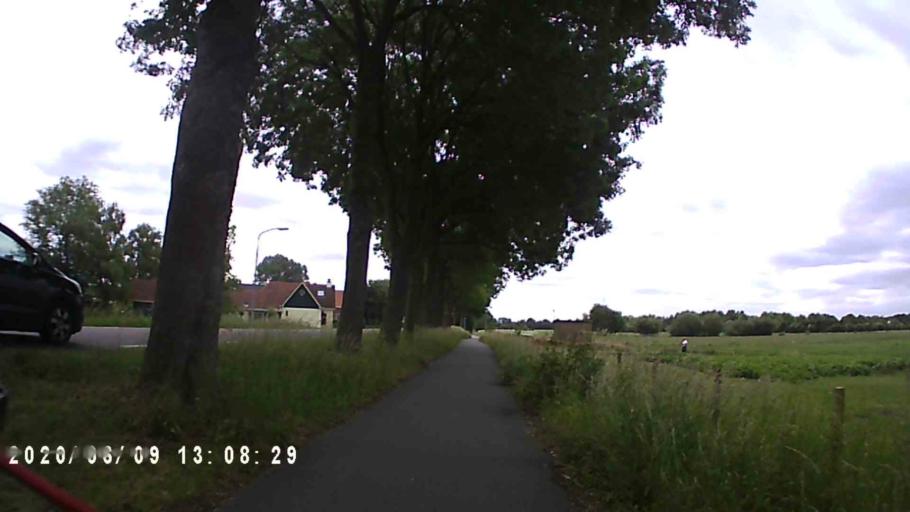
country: NL
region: Groningen
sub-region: Gemeente Haren
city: Haren
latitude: 53.2152
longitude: 6.6513
